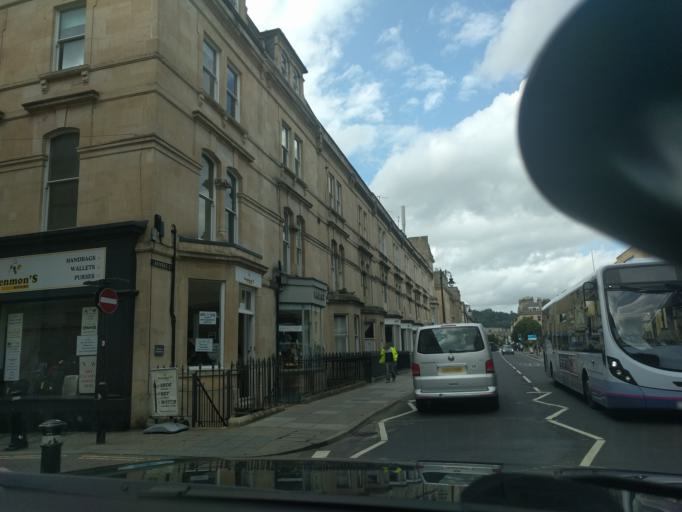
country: GB
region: England
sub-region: Bath and North East Somerset
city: Bath
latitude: 51.3786
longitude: -2.3571
